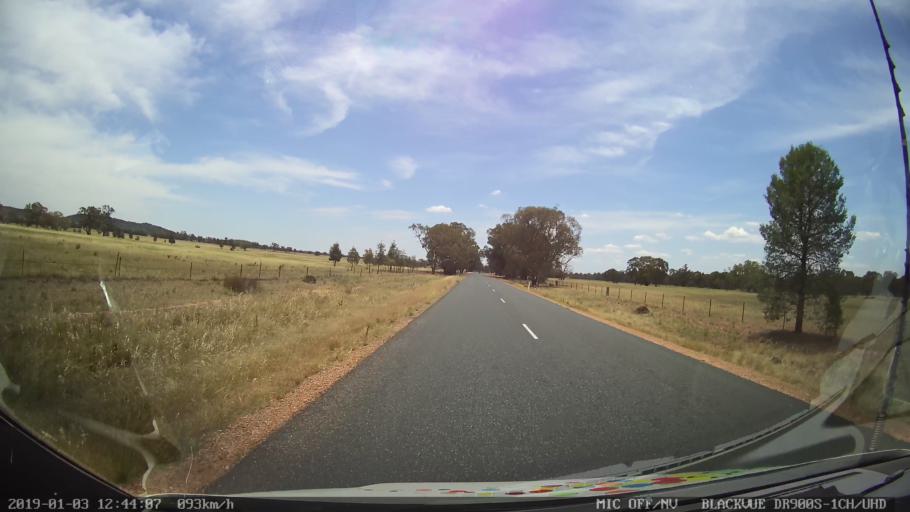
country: AU
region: New South Wales
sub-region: Weddin
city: Grenfell
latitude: -33.7659
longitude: 148.2149
